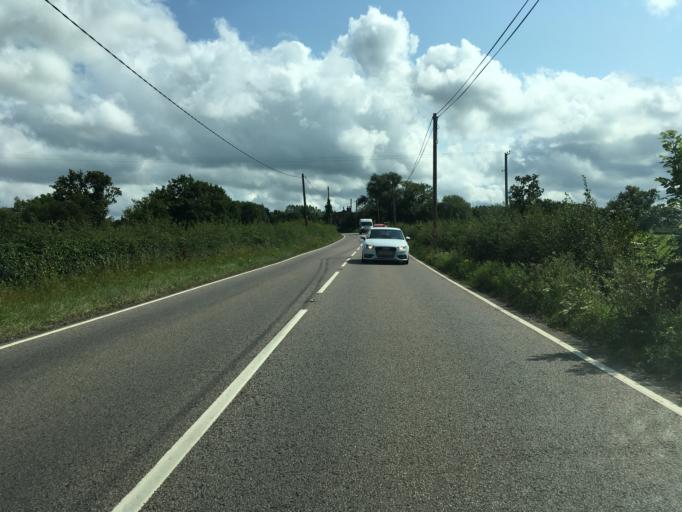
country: GB
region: England
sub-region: Kent
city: Headcorn
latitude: 51.1369
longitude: 0.6416
